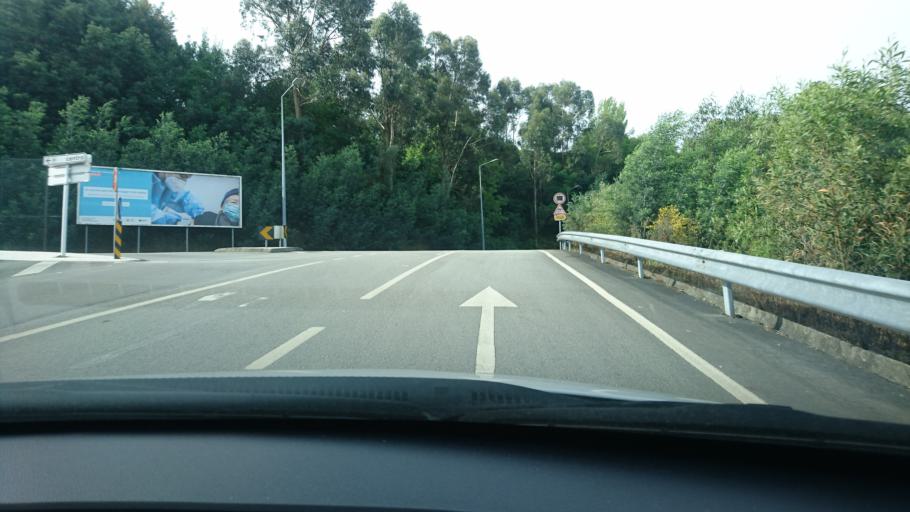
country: PT
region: Aveiro
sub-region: Oliveira de Azemeis
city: Oliveira de Azemeis
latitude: 40.8448
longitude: -8.4782
